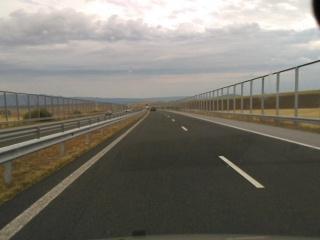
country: BG
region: Sliven
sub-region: Obshtina Sliven
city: Kermen
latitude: 42.5165
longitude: 26.3745
